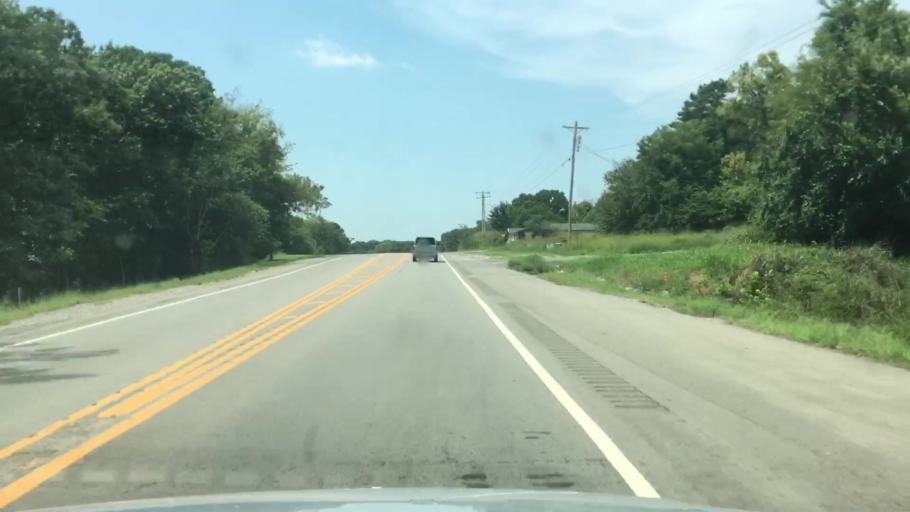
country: US
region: Oklahoma
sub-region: Wagoner County
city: Wagoner
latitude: 35.9297
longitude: -95.2482
